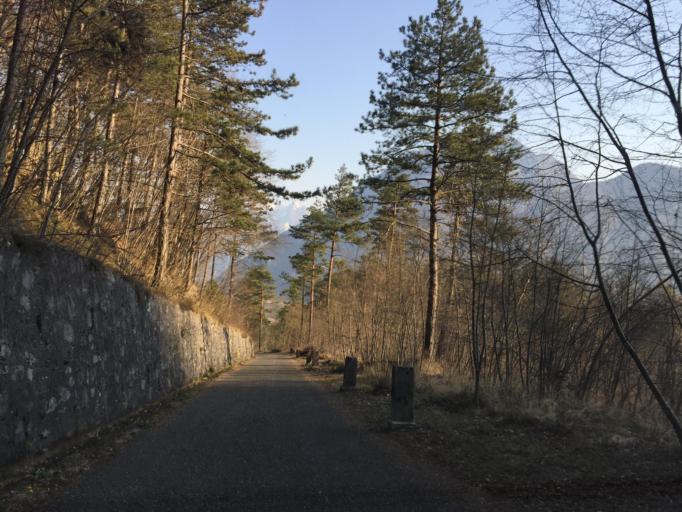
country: IT
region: Friuli Venezia Giulia
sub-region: Provincia di Udine
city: Amaro
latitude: 46.3824
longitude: 13.0858
